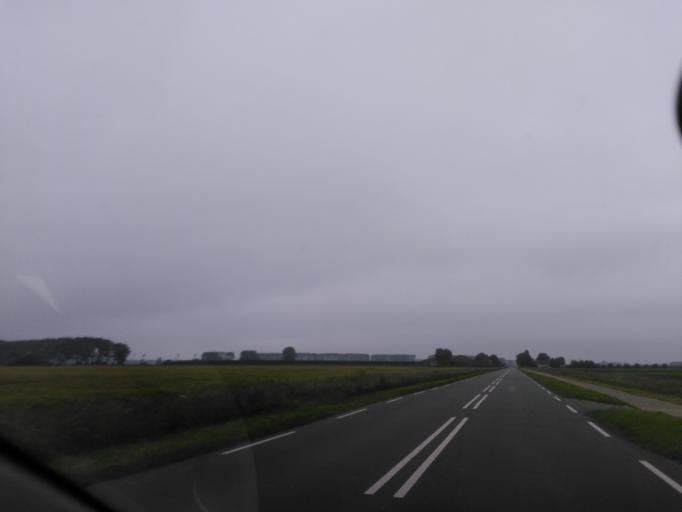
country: BE
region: Flanders
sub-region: Provincie Oost-Vlaanderen
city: Sint-Gillis-Waas
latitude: 51.2771
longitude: 4.1165
